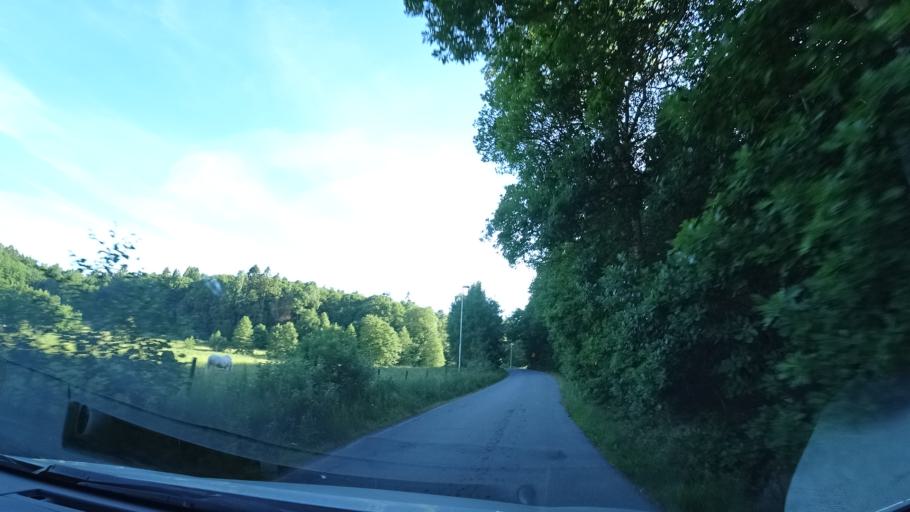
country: SE
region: Vaestra Goetaland
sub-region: Goteborg
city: Billdal
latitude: 57.5827
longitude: 11.9856
